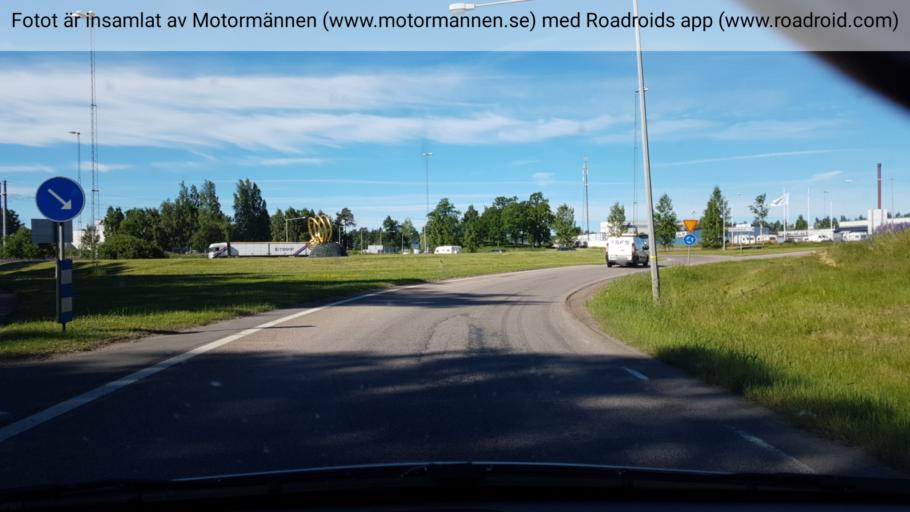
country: SE
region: Vaestra Goetaland
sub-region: Skovde Kommun
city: Skoevde
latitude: 58.3825
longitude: 13.8728
